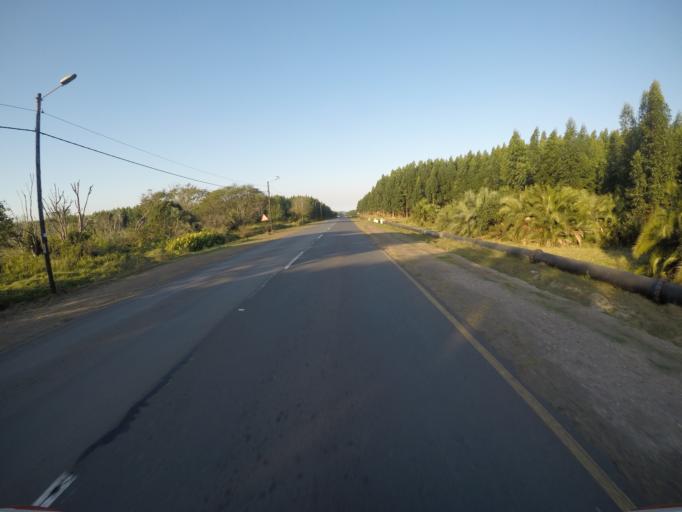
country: ZA
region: KwaZulu-Natal
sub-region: uThungulu District Municipality
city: KwaMbonambi
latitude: -28.6832
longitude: 32.1654
